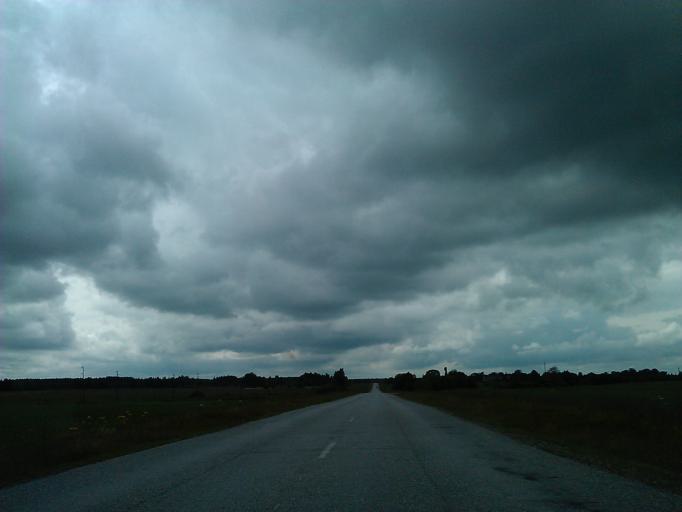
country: LV
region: Aizpute
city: Aizpute
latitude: 56.8033
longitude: 21.6915
